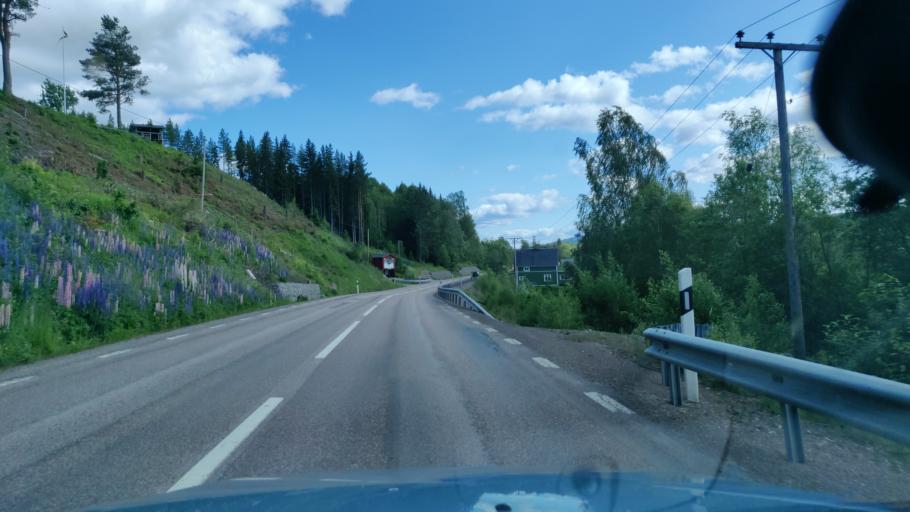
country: SE
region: Vaermland
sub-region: Torsby Kommun
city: Torsby
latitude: 60.5781
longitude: 13.0846
